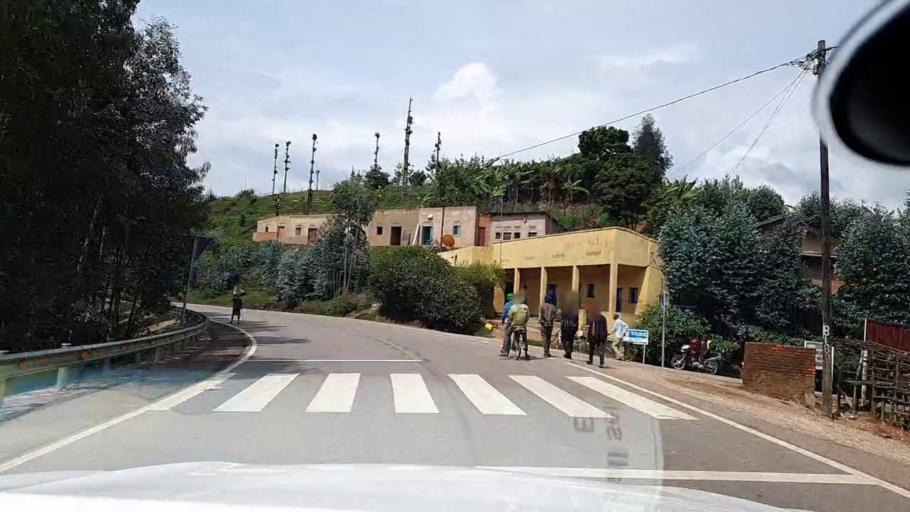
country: RW
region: Southern Province
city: Nzega
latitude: -2.4834
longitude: 29.5201
